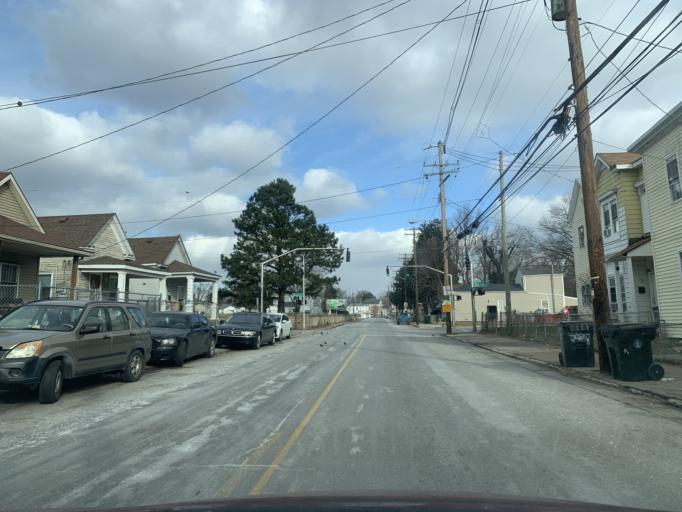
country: US
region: Kentucky
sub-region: Jefferson County
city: Louisville
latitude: 38.2630
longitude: -85.7933
